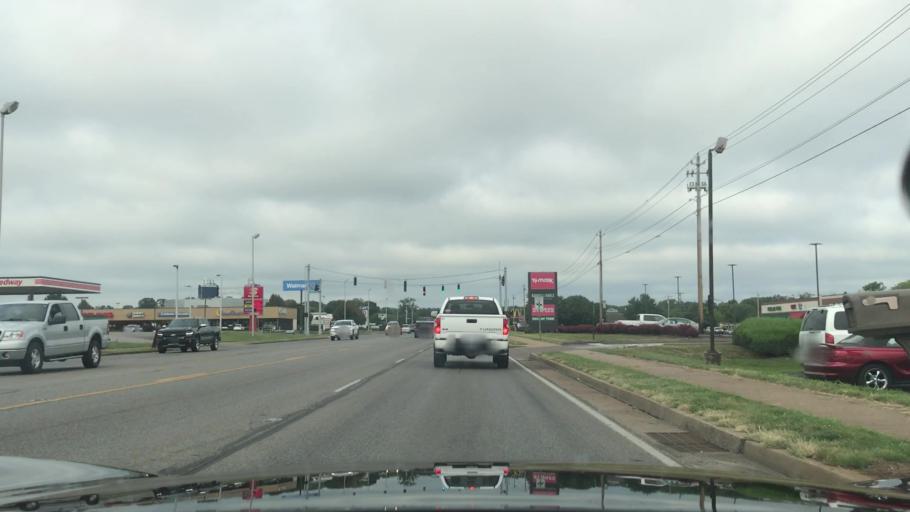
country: US
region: Kentucky
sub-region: Warren County
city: Bowling Green
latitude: 36.9524
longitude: -86.4340
